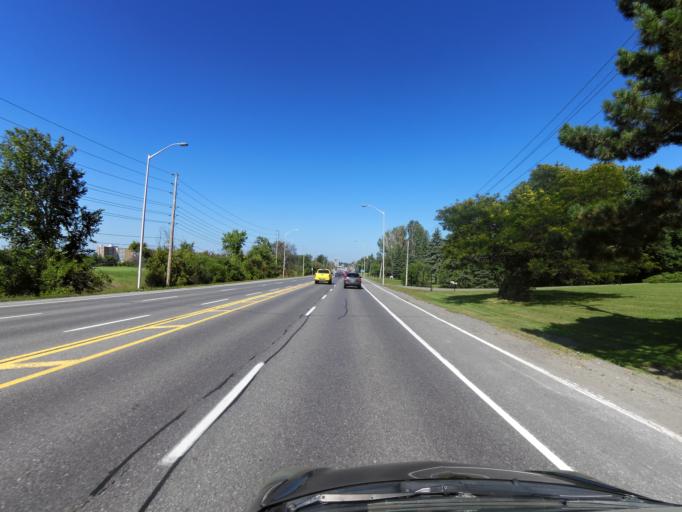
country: CA
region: Ontario
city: Bells Corners
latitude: 45.3383
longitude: -75.8103
